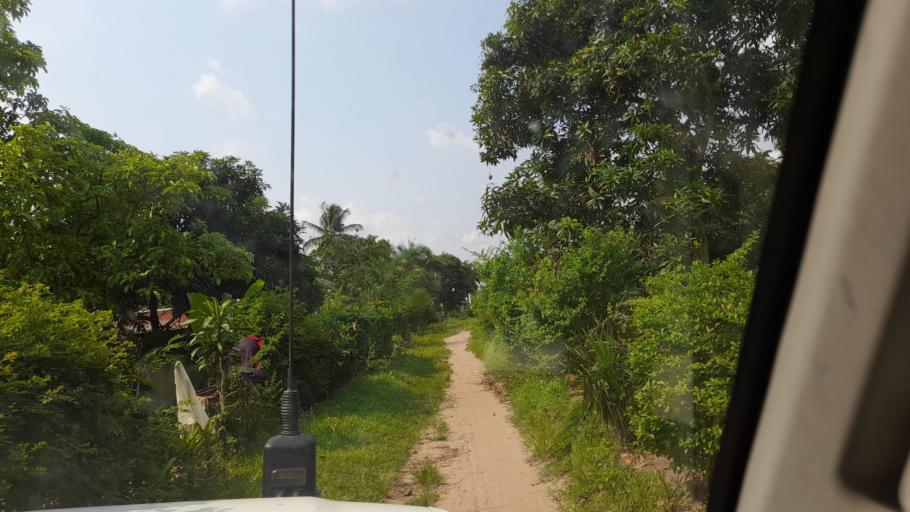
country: CD
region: Kasai-Occidental
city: Kananga
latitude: -5.9179
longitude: 22.4773
